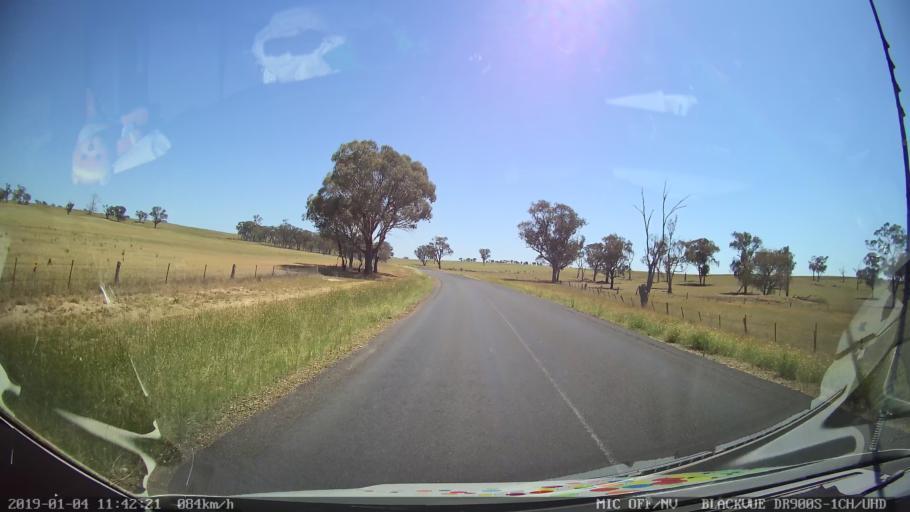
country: AU
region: New South Wales
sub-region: Cabonne
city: Molong
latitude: -32.9826
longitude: 148.7867
